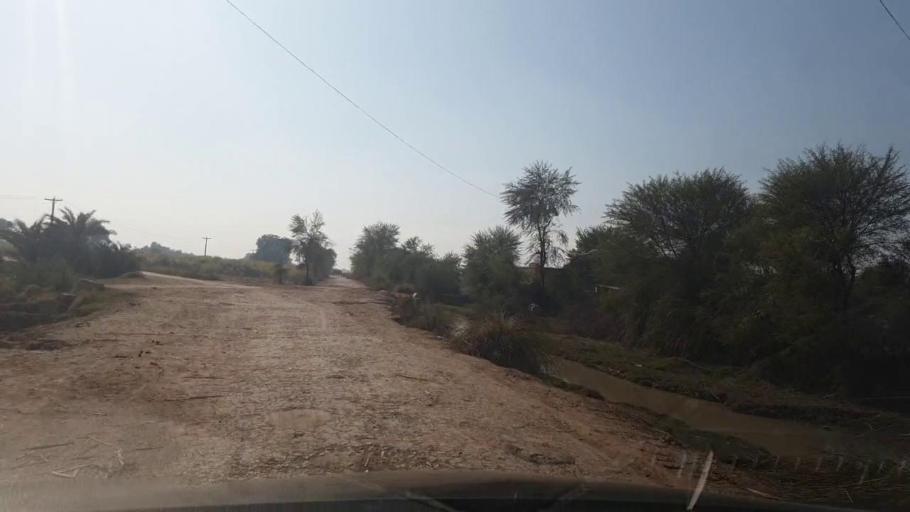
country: PK
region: Sindh
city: Ubauro
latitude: 28.1483
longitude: 69.6907
